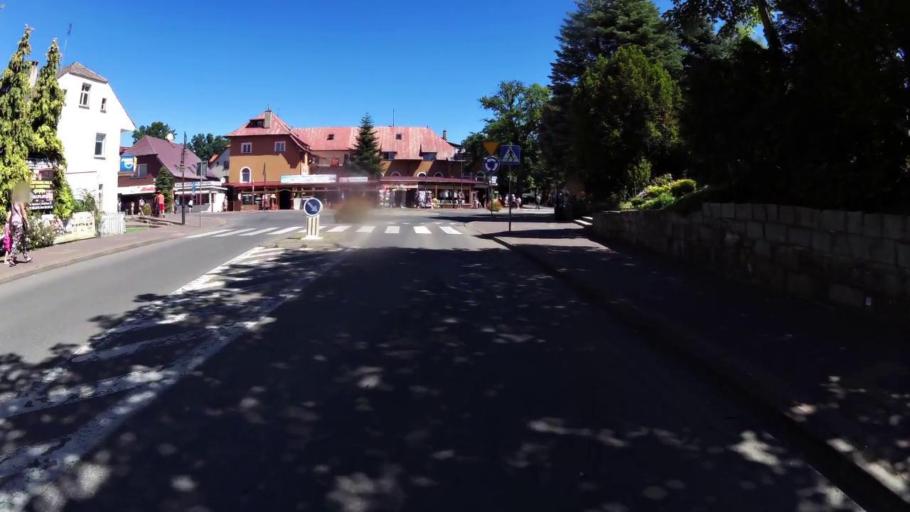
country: PL
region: West Pomeranian Voivodeship
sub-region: Powiat gryficki
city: Rewal
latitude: 54.0809
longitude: 15.0147
